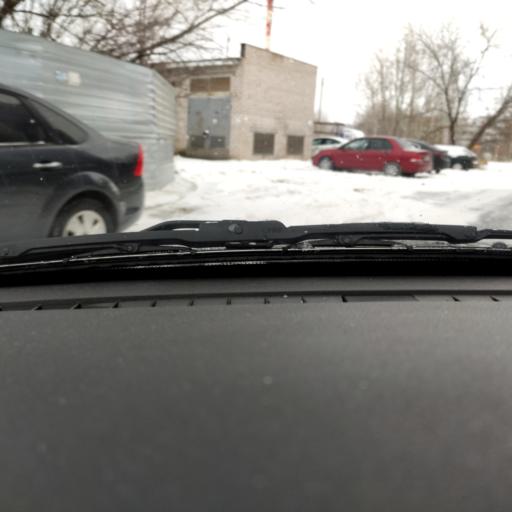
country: RU
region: Voronezj
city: Novaya Usman'
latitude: 51.6087
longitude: 39.3711
